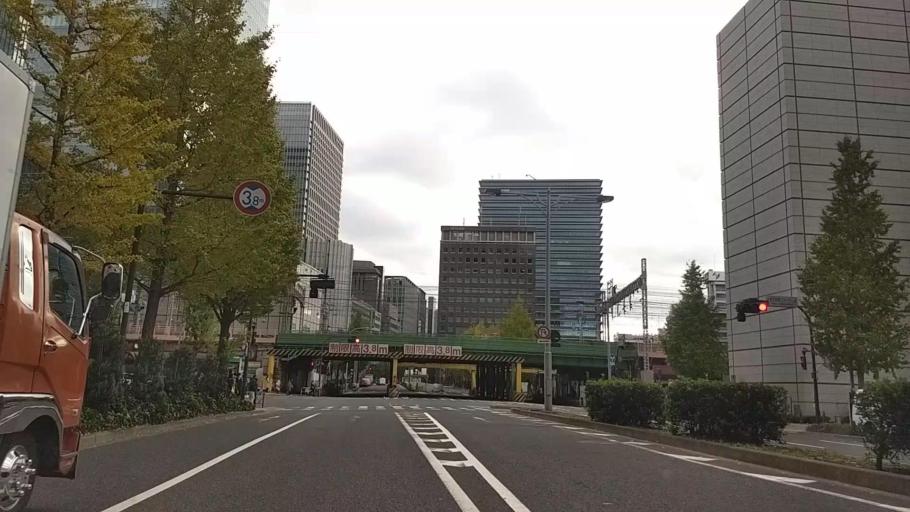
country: JP
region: Tokyo
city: Tokyo
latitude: 35.6778
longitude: 139.7644
